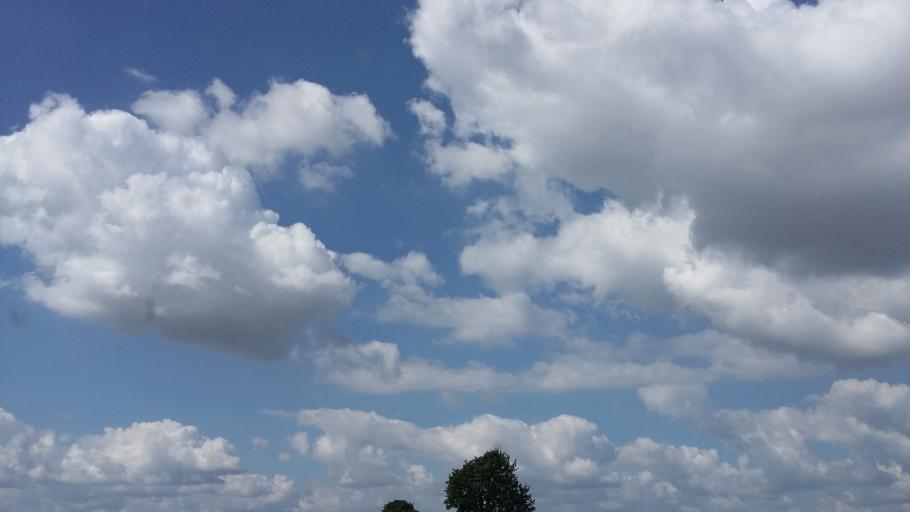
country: DE
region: Bavaria
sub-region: Swabia
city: Pfaffenhofen an der Roth
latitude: 48.3517
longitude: 10.2091
